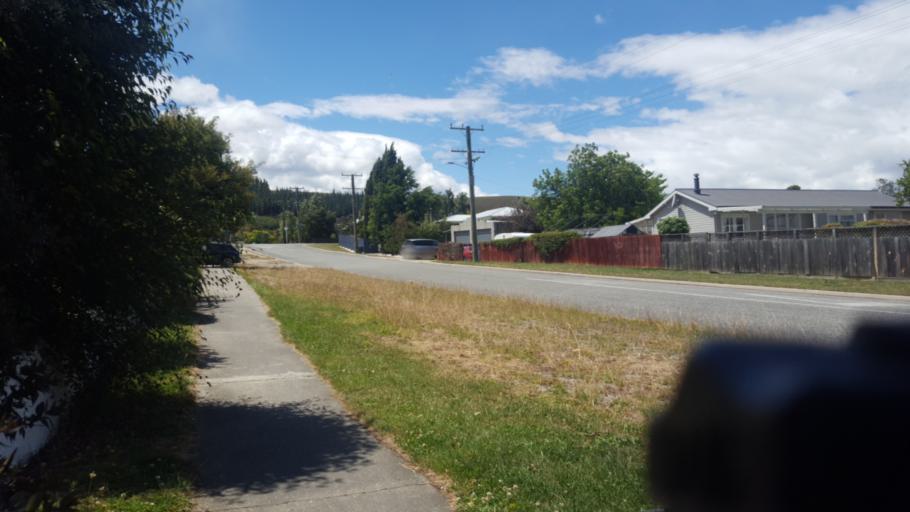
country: NZ
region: Otago
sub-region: Queenstown-Lakes District
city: Wanaka
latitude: -45.1904
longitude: 169.3213
